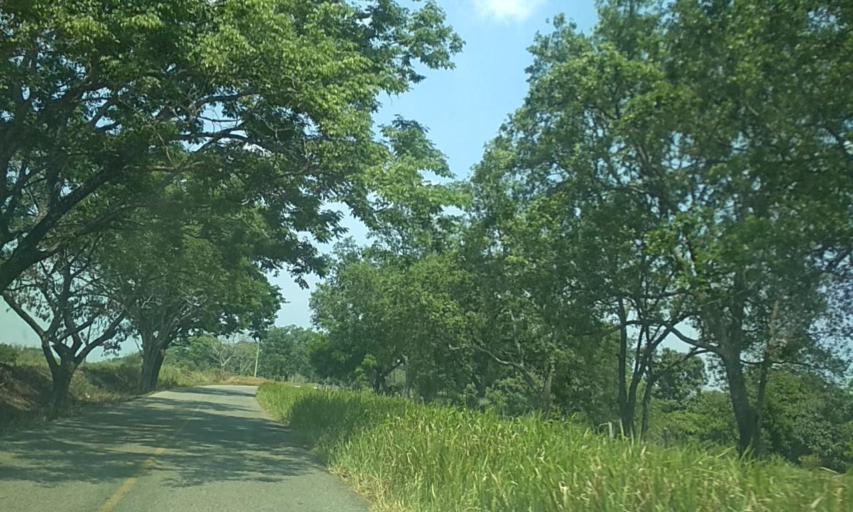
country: MX
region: Tabasco
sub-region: Cardenas
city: Poblado C-33 20 de Noviembre
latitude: 17.8526
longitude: -93.5780
